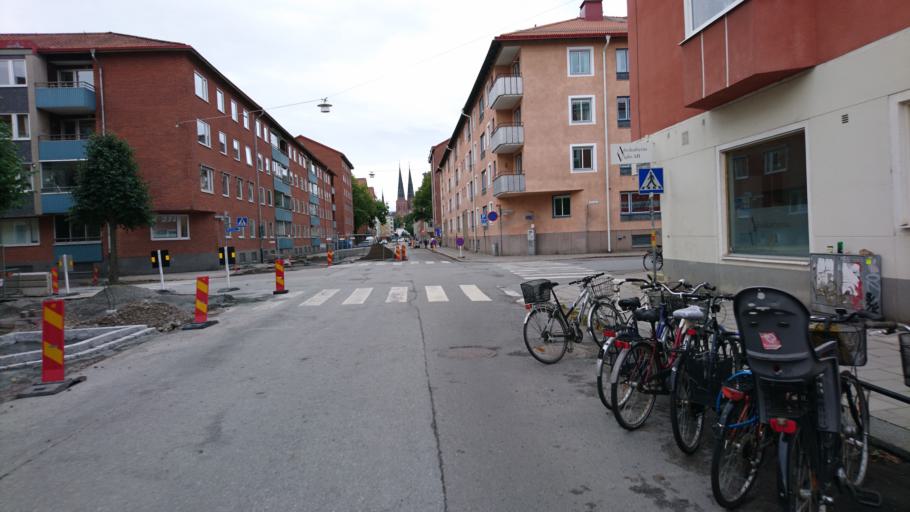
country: SE
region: Uppsala
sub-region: Uppsala Kommun
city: Uppsala
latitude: 59.8639
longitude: 17.6222
